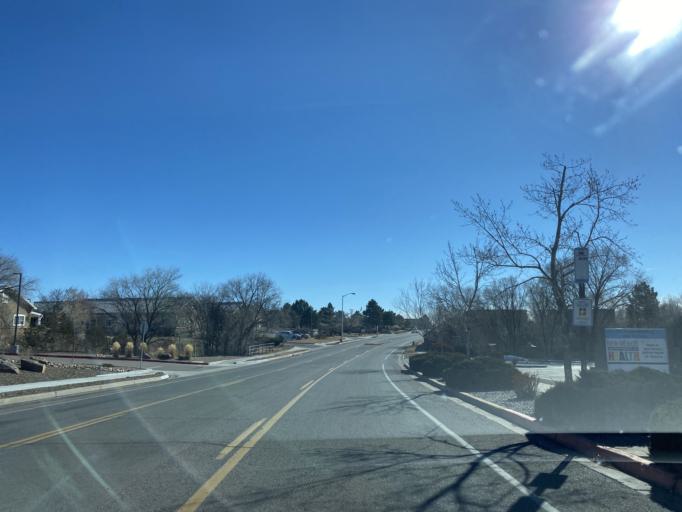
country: US
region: New Mexico
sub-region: Santa Fe County
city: Santa Fe
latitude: 35.6568
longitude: -105.9589
